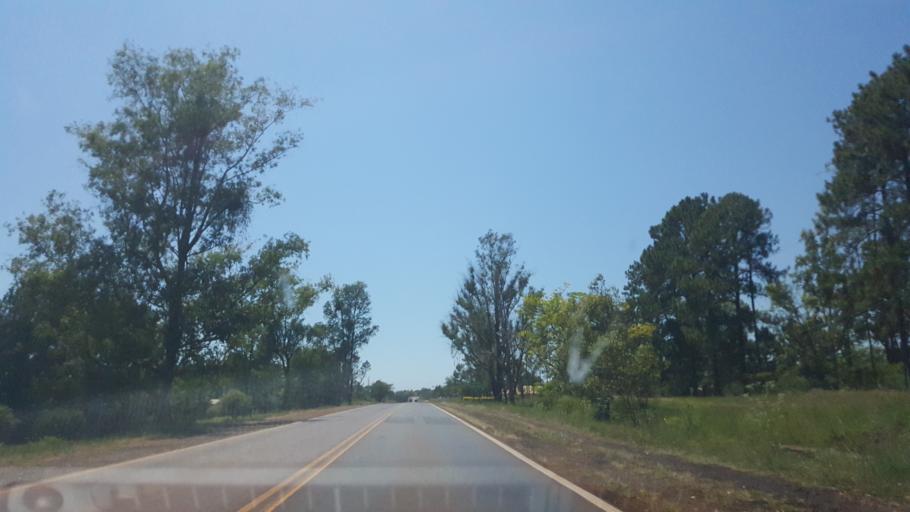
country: AR
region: Corrientes
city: Santo Tome
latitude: -28.5471
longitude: -56.0820
